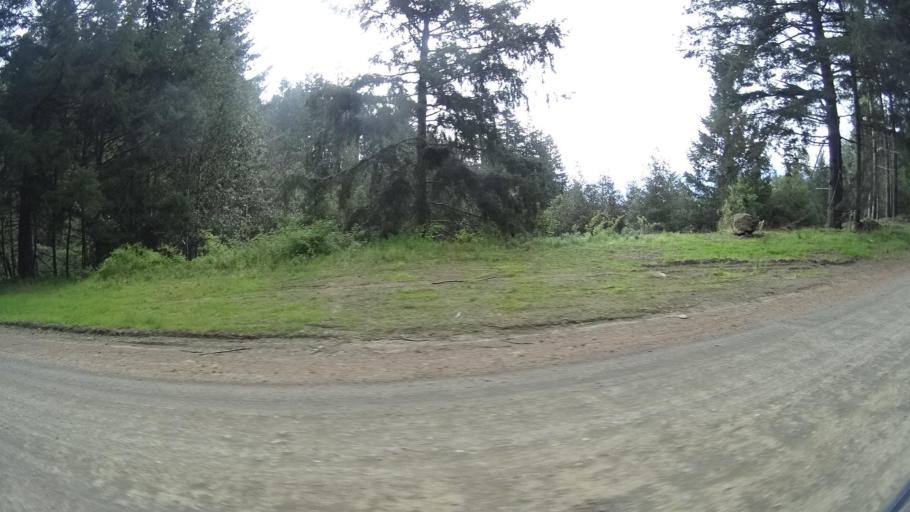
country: US
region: California
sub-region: Humboldt County
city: Redway
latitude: 40.2662
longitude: -123.7695
